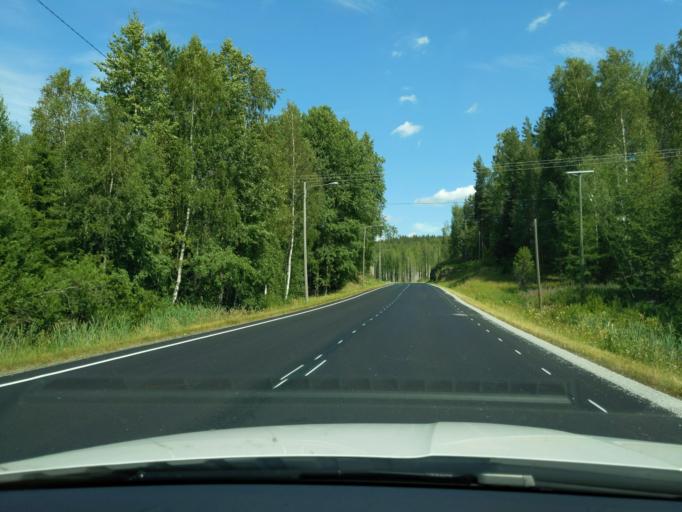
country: FI
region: Paijanne Tavastia
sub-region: Lahti
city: Nastola
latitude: 61.0739
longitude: 25.8252
